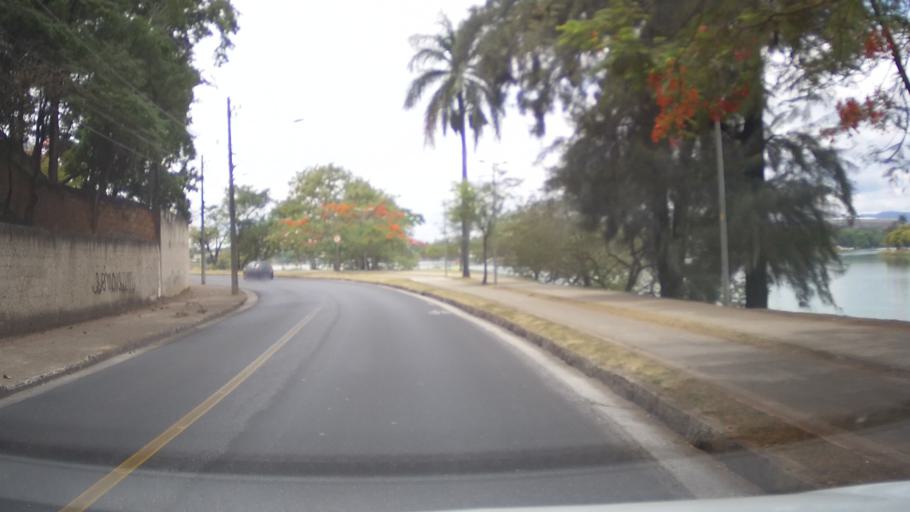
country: BR
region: Minas Gerais
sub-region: Belo Horizonte
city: Belo Horizonte
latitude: -19.8506
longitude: -43.9824
